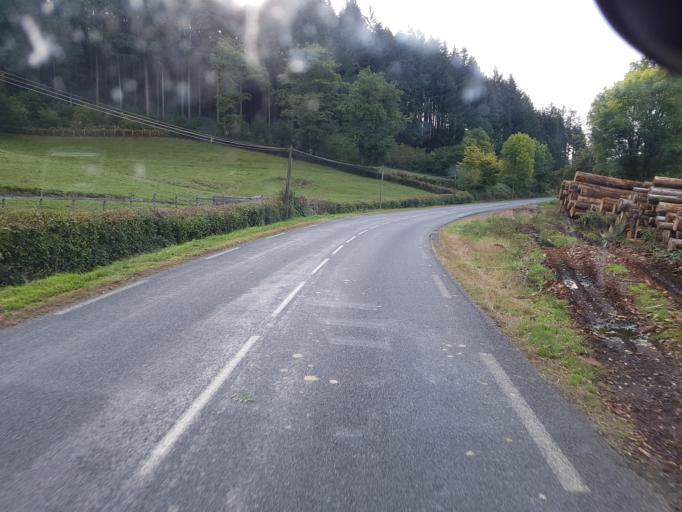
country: FR
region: Bourgogne
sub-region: Departement de Saone-et-Loire
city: Chauffailles
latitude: 46.2258
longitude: 4.4252
